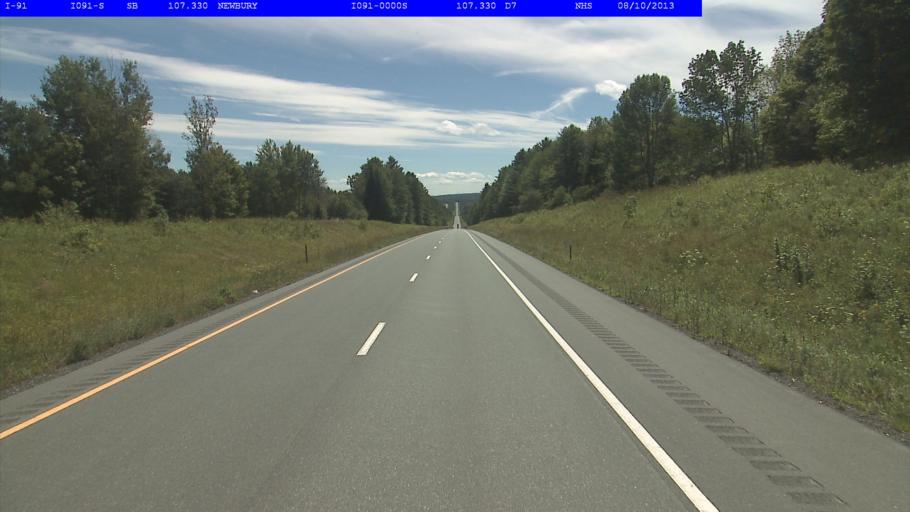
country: US
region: New Hampshire
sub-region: Grafton County
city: Woodsville
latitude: 44.1193
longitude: -72.1058
